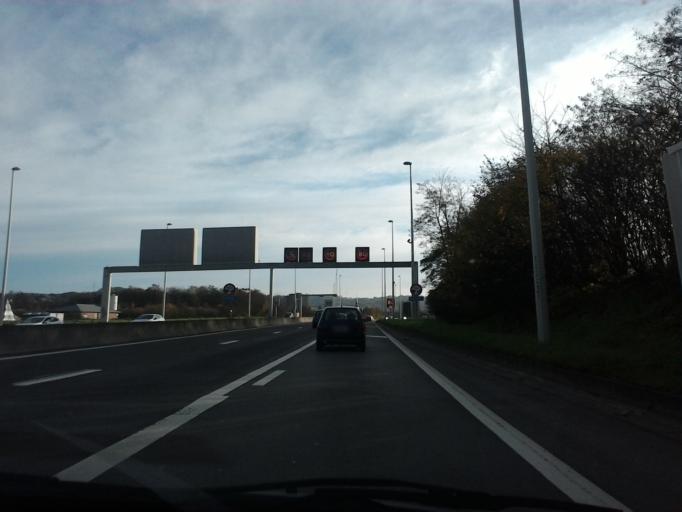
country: BE
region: Wallonia
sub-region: Province de Liege
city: Chaudfontaine
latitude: 50.6126
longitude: 5.6046
